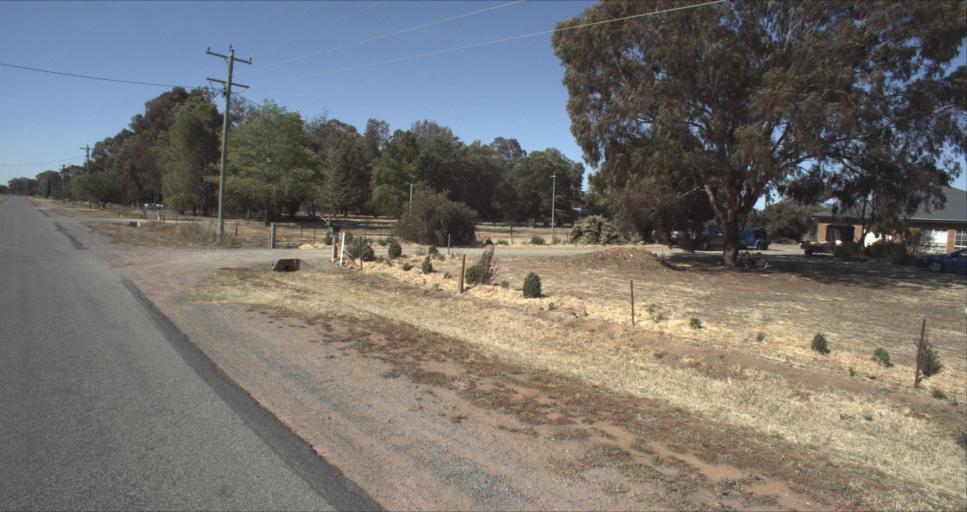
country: AU
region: New South Wales
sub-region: Leeton
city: Leeton
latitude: -34.5414
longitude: 146.4190
